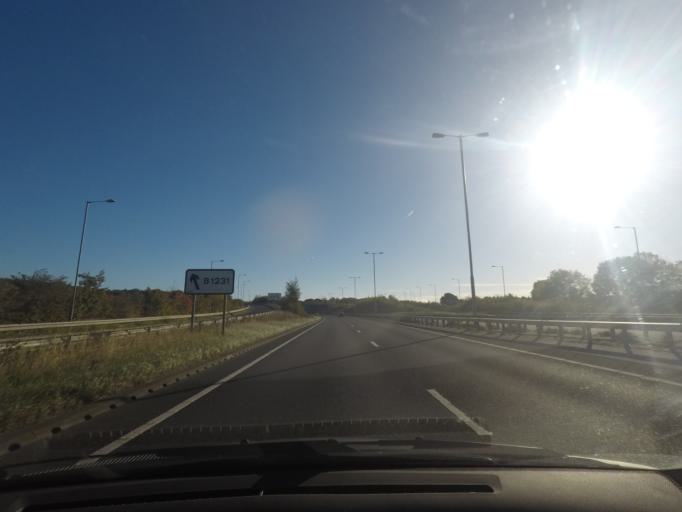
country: GB
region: England
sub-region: East Riding of Yorkshire
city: North Ferriby
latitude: 53.7248
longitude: -0.5245
